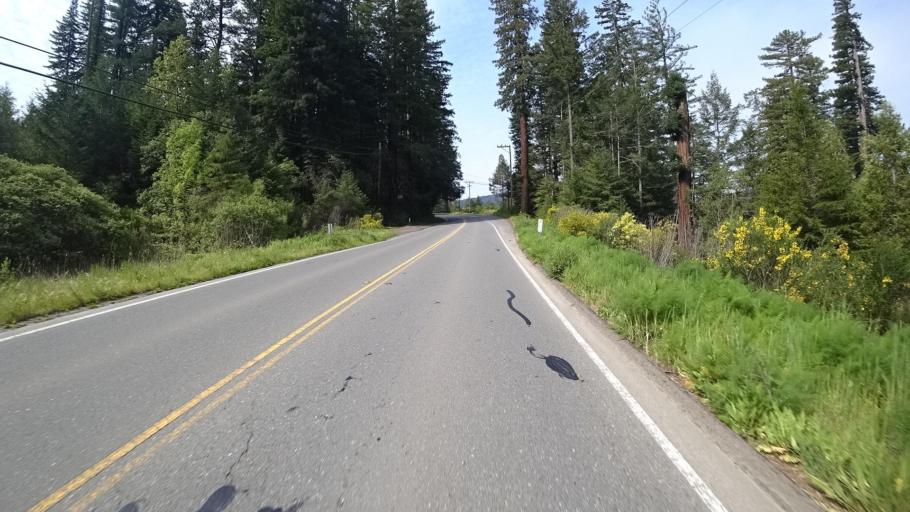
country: US
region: California
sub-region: Humboldt County
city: Redway
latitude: 40.1288
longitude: -123.8196
